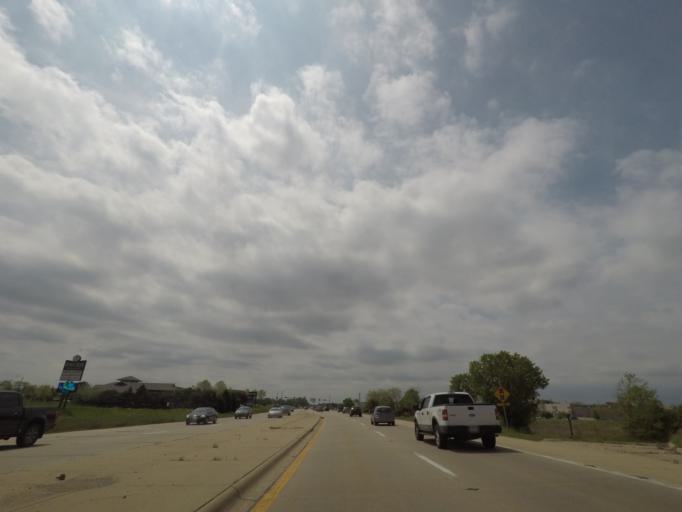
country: US
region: Illinois
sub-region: Winnebago County
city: Cherry Valley
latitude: 42.2992
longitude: -88.9800
